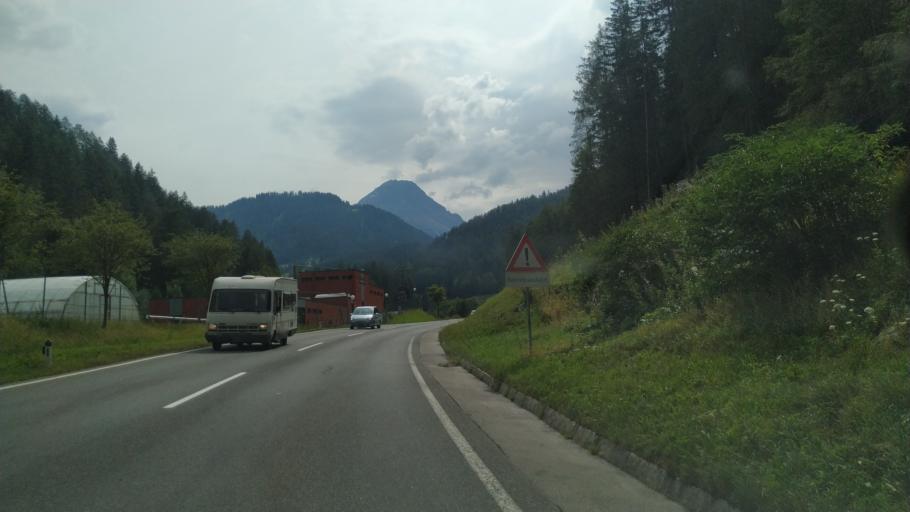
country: AT
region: Tyrol
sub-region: Politischer Bezirk Landeck
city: Nauders
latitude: 46.9079
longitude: 10.4961
